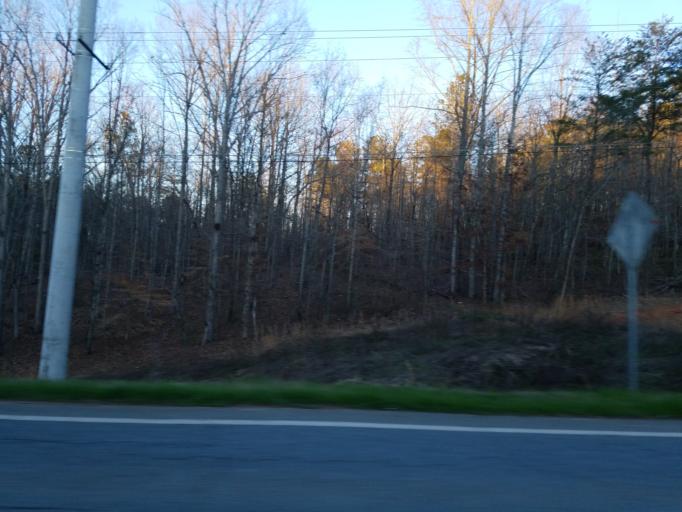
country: US
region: Georgia
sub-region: Dawson County
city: Dawsonville
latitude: 34.3278
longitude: -84.0094
